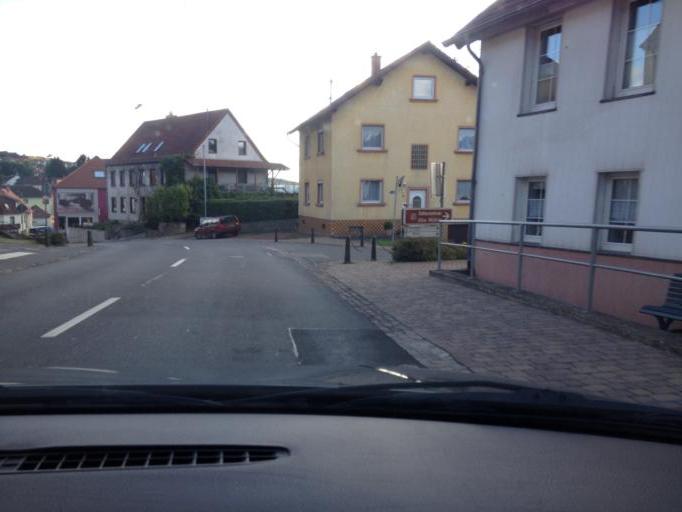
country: DE
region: Saarland
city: Marpingen
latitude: 49.4532
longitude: 7.0577
